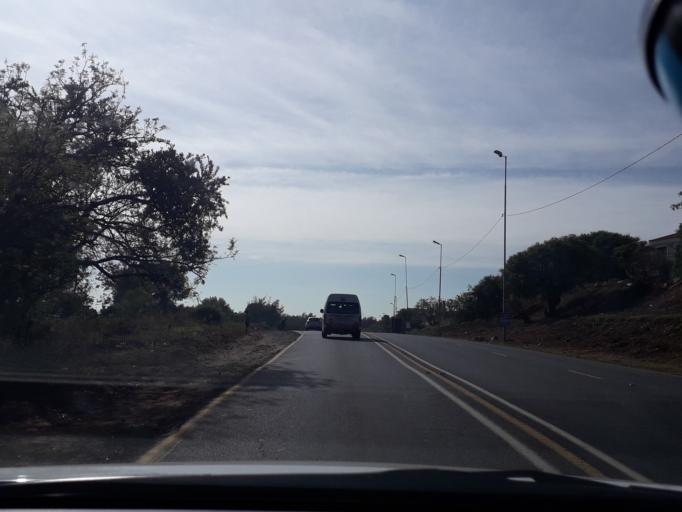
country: ZA
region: Gauteng
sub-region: City of Johannesburg Metropolitan Municipality
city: Roodepoort
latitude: -26.1308
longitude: 27.8976
